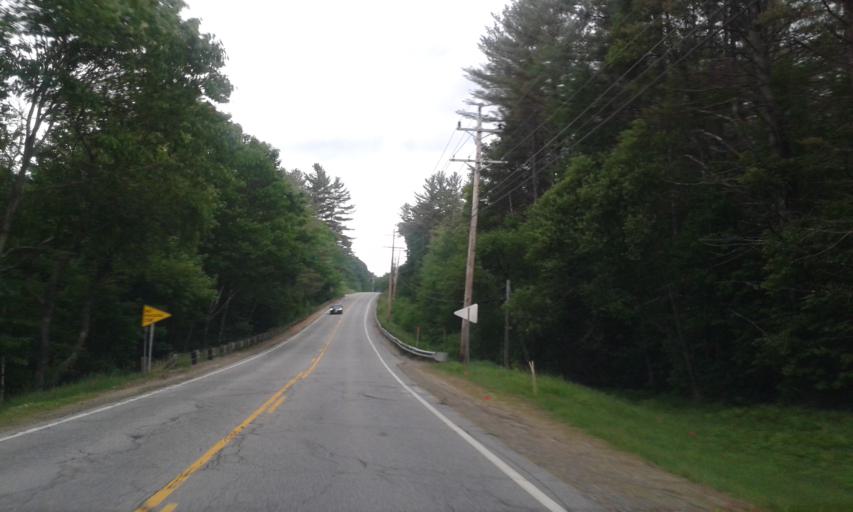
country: US
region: New Hampshire
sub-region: Grafton County
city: Woodstock
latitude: 44.0028
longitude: -71.6844
